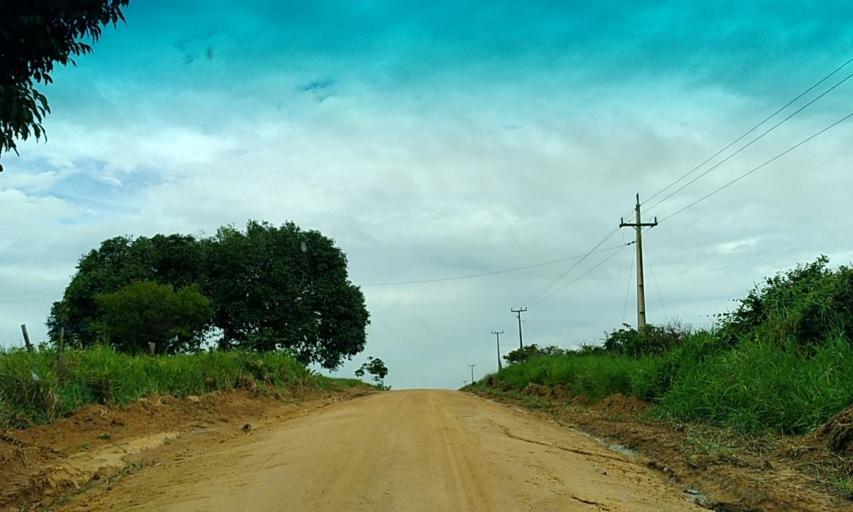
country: BR
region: Para
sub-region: Senador Jose Porfirio
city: Senador Jose Porfirio
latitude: -3.0277
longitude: -51.6811
